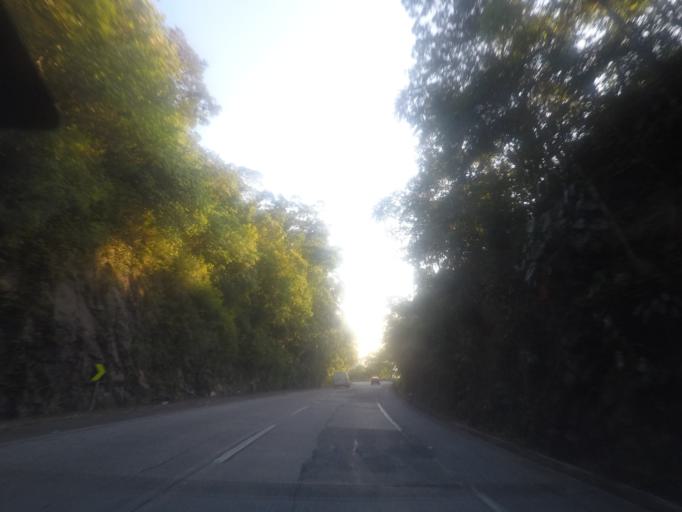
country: BR
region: Rio de Janeiro
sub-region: Petropolis
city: Petropolis
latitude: -22.5374
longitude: -43.2326
